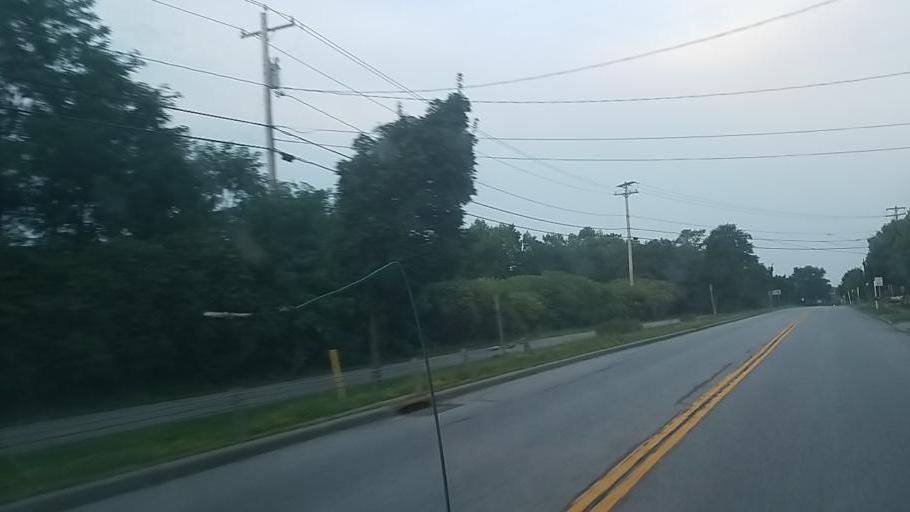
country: US
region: New York
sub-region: Montgomery County
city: Fonda
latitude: 42.9475
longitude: -74.3775
